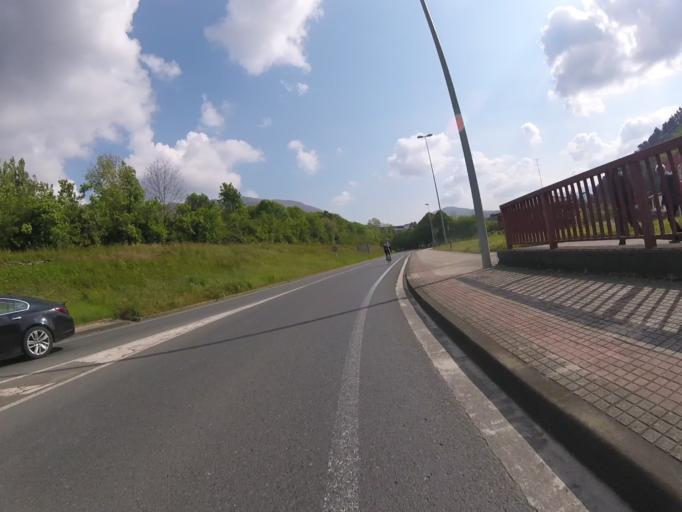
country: ES
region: Basque Country
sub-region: Provincia de Guipuzcoa
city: Azkoitia
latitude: 43.1731
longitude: -2.3028
